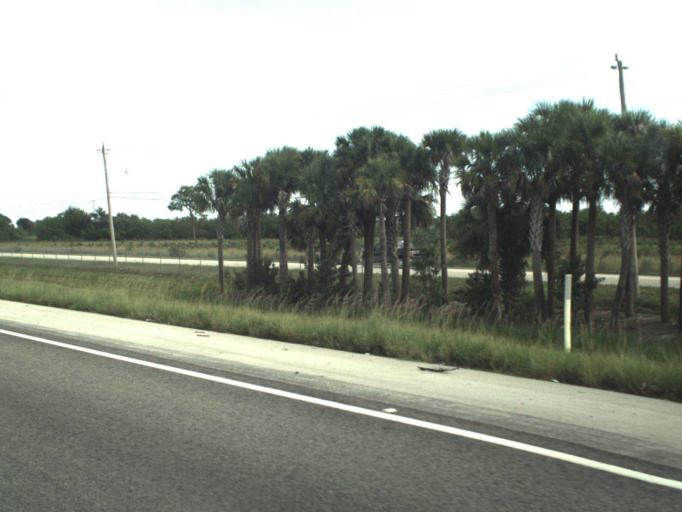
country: US
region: Florida
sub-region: Saint Lucie County
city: Lakewood Park
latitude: 27.5267
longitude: -80.4544
